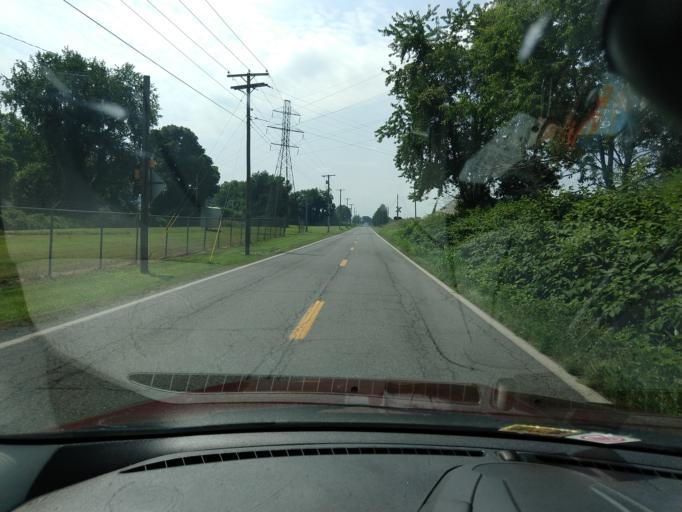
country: US
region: West Virginia
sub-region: Mason County
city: New Haven
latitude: 38.9628
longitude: -81.9266
